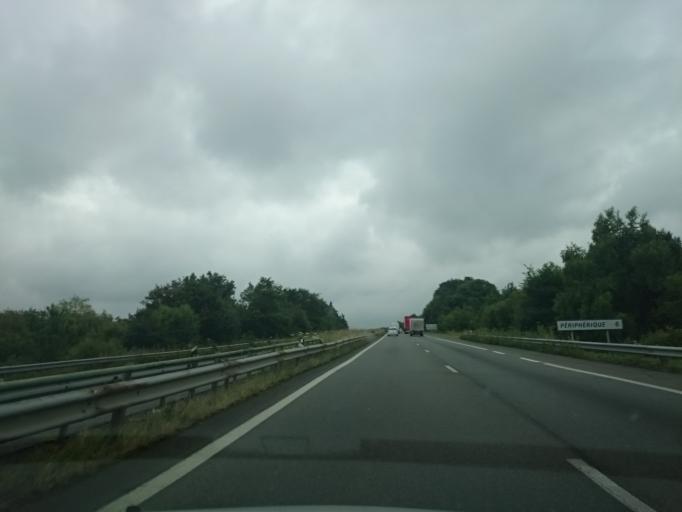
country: FR
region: Pays de la Loire
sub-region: Departement de la Loire-Atlantique
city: Sautron
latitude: 47.2522
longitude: -1.6794
